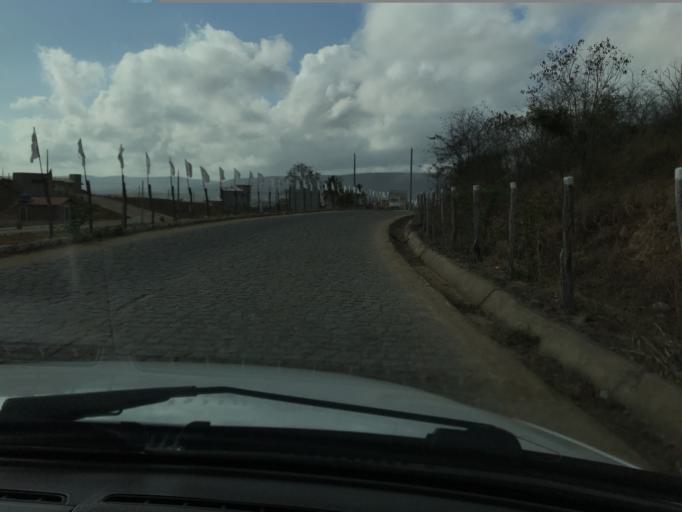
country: BR
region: Pernambuco
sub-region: Bezerros
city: Bezerros
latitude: -8.2150
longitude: -35.7534
